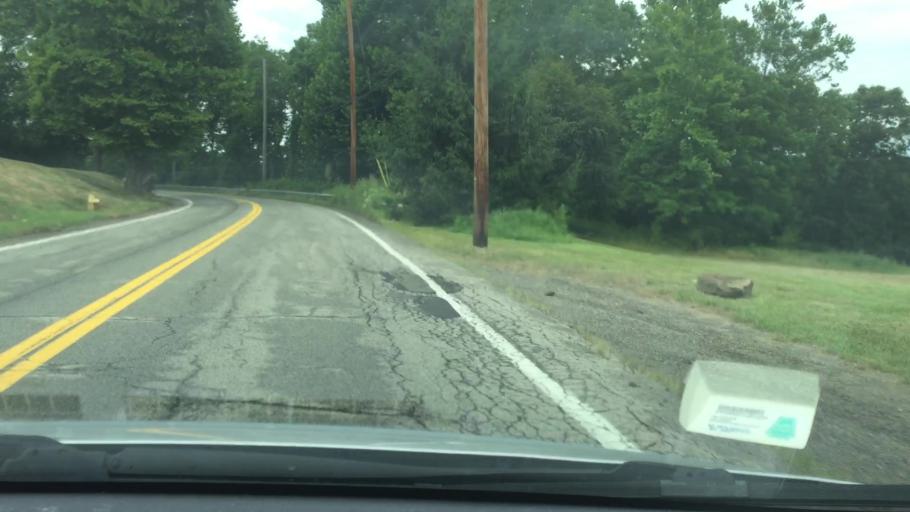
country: US
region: Pennsylvania
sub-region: Allegheny County
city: Allison Park
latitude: 40.5659
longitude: -79.9757
